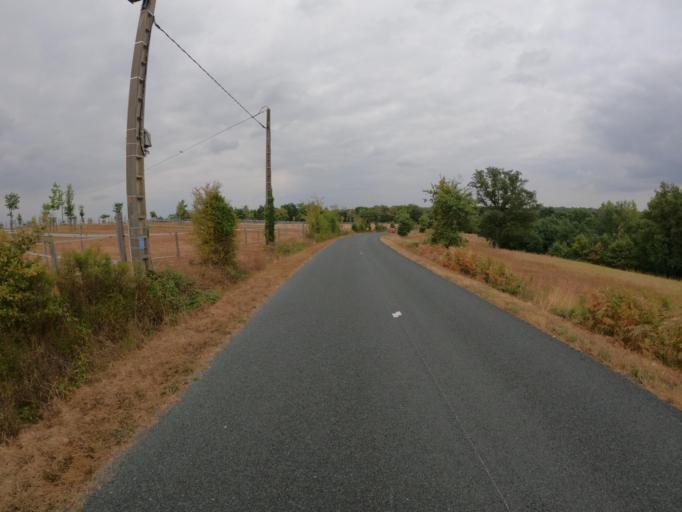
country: FR
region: Pays de la Loire
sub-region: Departement de la Vendee
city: Tiffauges
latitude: 46.9897
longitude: -1.1098
